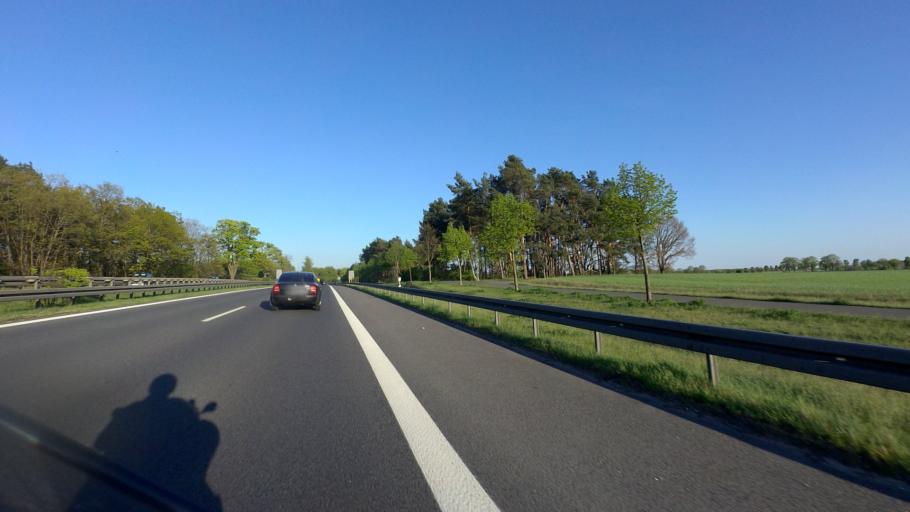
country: DE
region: Brandenburg
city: Falkensee
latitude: 52.5303
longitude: 13.0980
